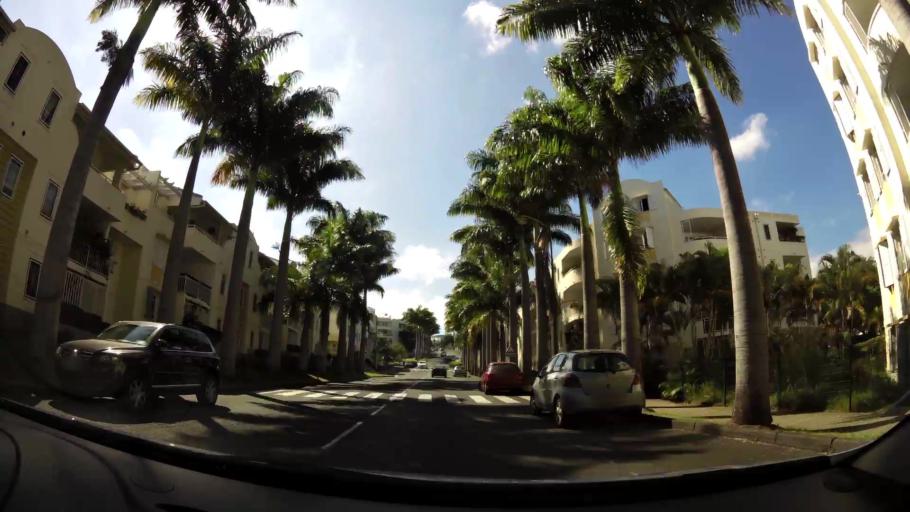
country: RE
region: Reunion
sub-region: Reunion
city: Le Tampon
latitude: -21.2768
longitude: 55.5038
